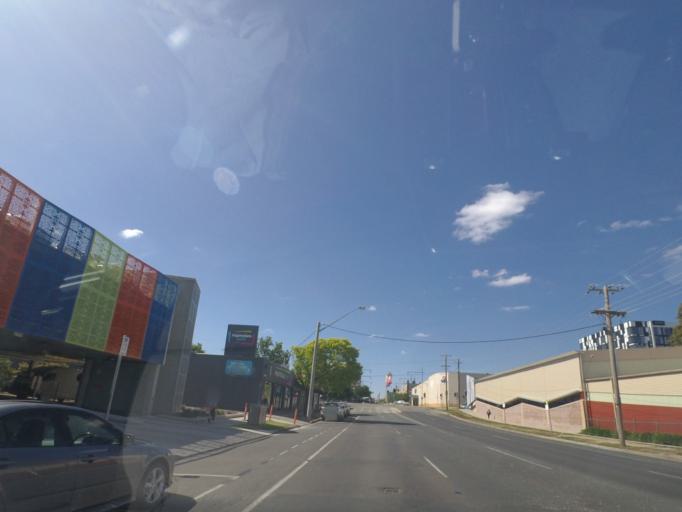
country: AU
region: New South Wales
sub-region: Albury Municipality
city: South Albury
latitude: -36.0836
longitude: 146.9150
